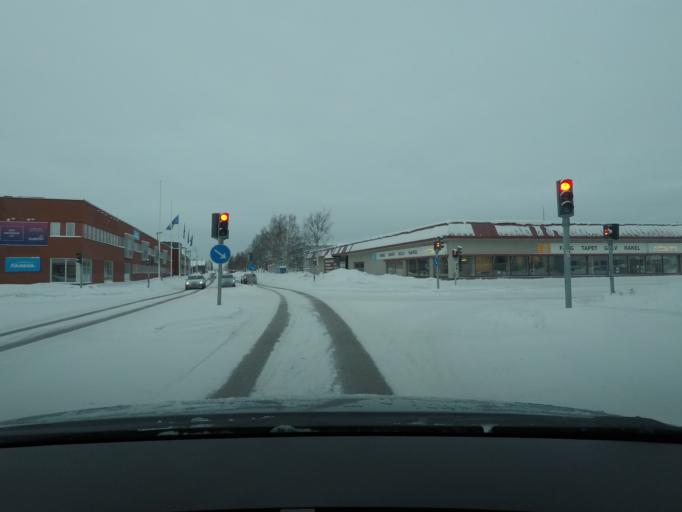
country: SE
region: Norrbotten
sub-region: Lulea Kommun
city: Lulea
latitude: 65.5992
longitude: 22.1439
